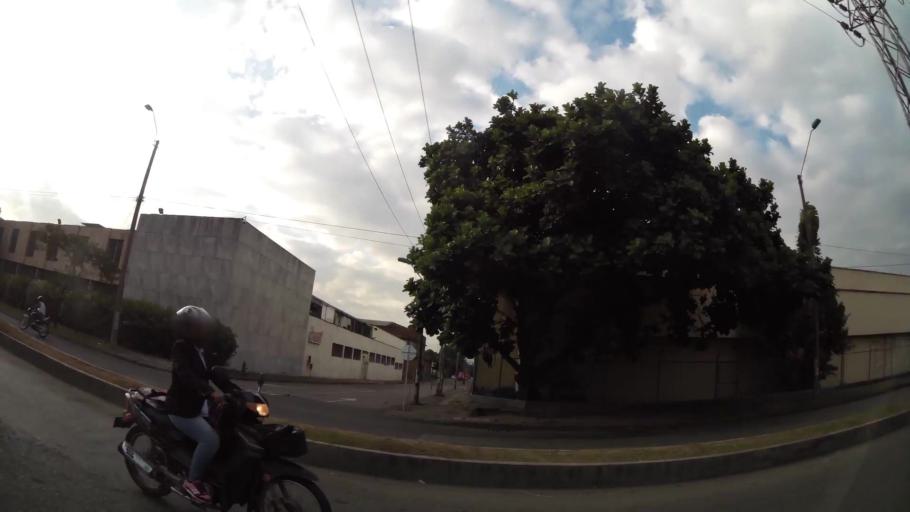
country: CO
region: Valle del Cauca
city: Cali
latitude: 3.4532
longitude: -76.5170
